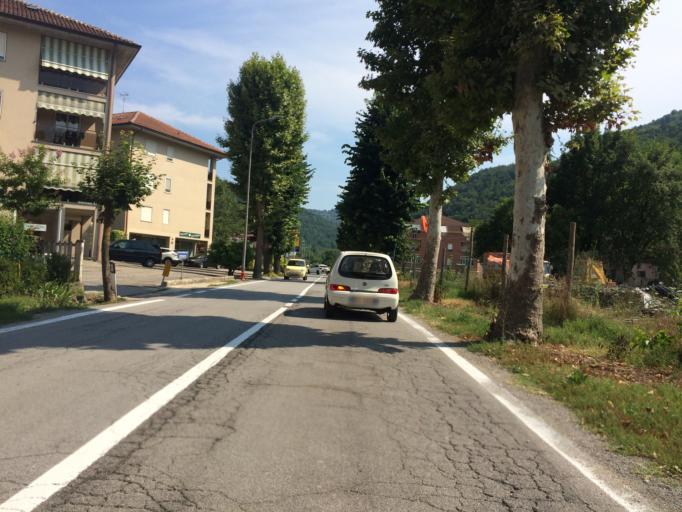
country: IT
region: Piedmont
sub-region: Provincia di Cuneo
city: Cortemilia
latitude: 44.5741
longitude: 8.1999
